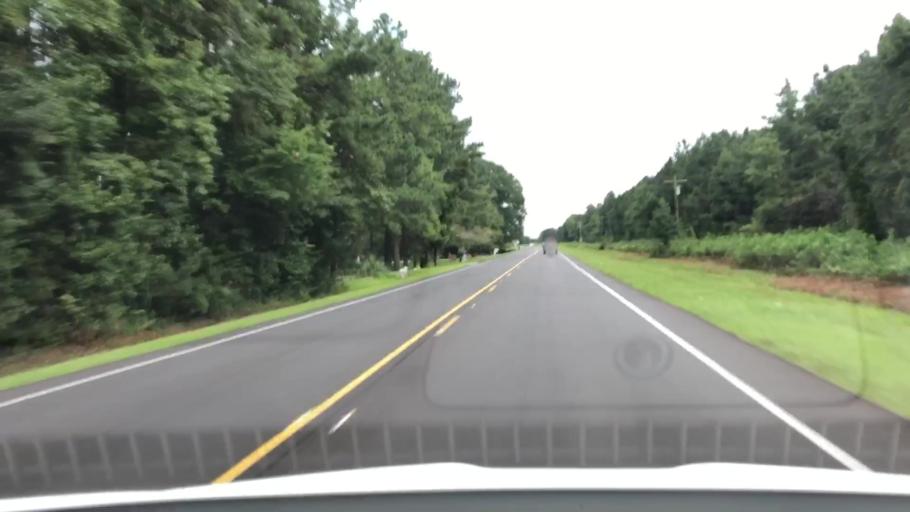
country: US
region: North Carolina
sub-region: Jones County
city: Maysville
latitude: 34.8885
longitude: -77.2137
